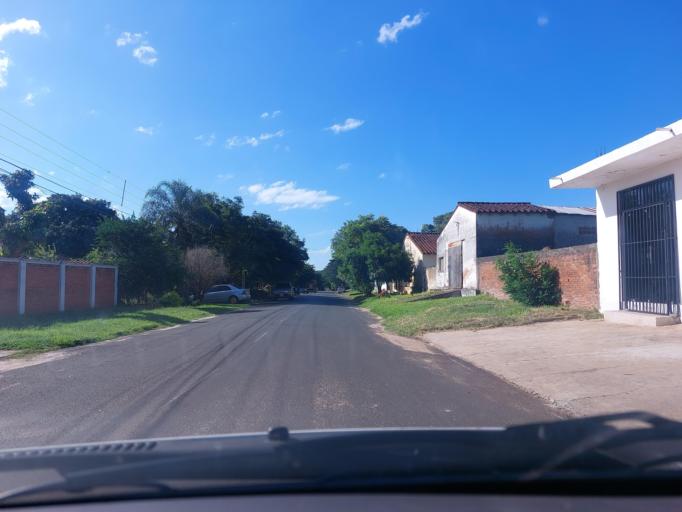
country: PY
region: San Pedro
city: Guayaybi
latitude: -24.6607
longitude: -56.4451
